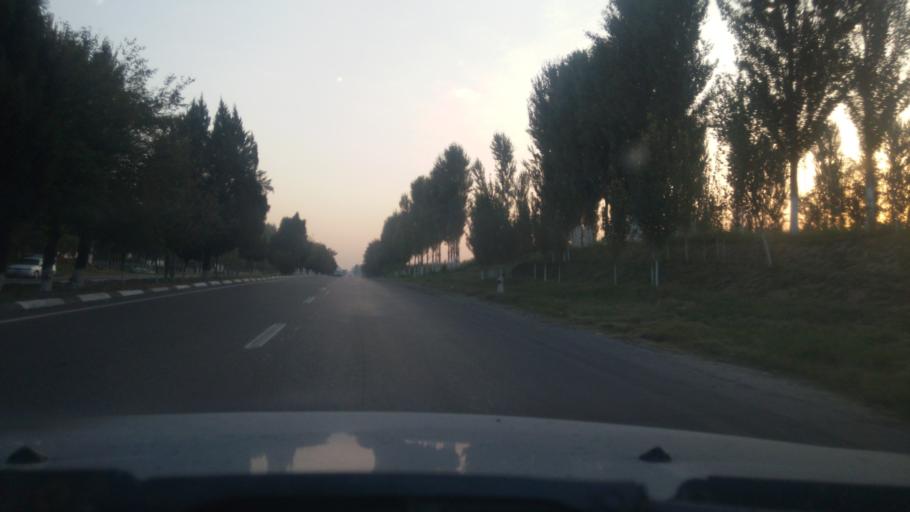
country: UZ
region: Toshkent
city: Amir Timur
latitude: 41.0748
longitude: 68.9300
